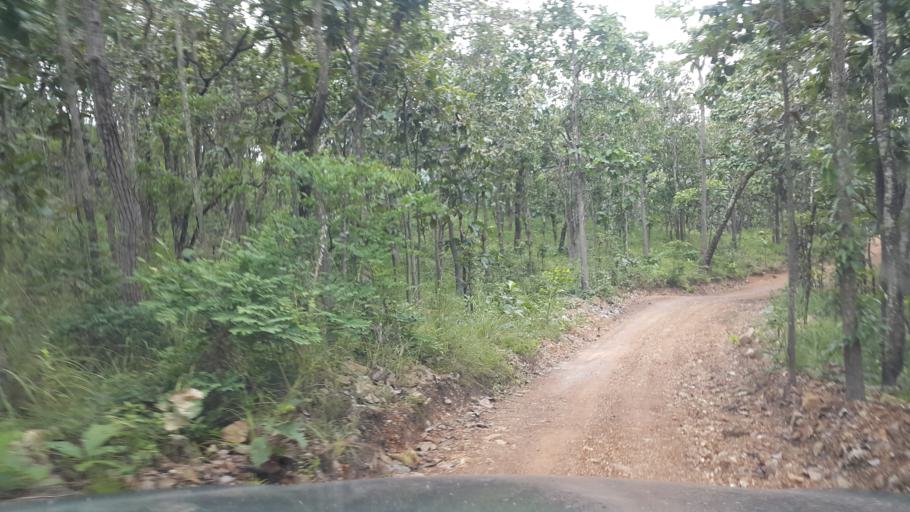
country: TH
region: Chiang Mai
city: San Sai
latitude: 18.9612
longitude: 99.1293
